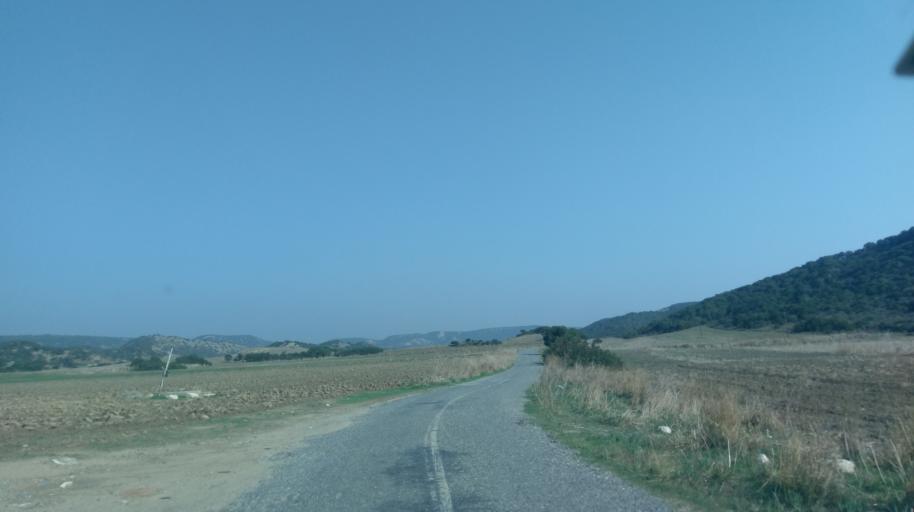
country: CY
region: Ammochostos
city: Rizokarpaso
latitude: 35.6381
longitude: 34.5124
